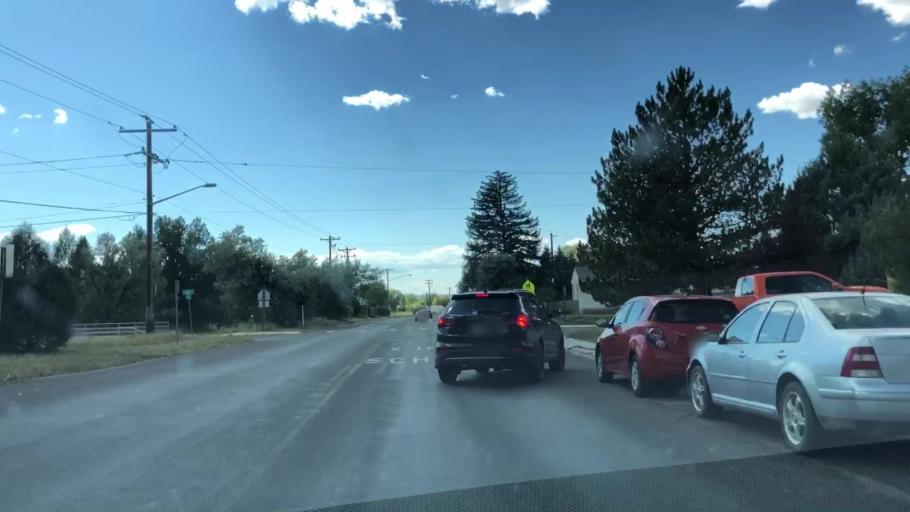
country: US
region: Wyoming
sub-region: Albany County
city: Laramie
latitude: 41.3029
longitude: -105.5807
